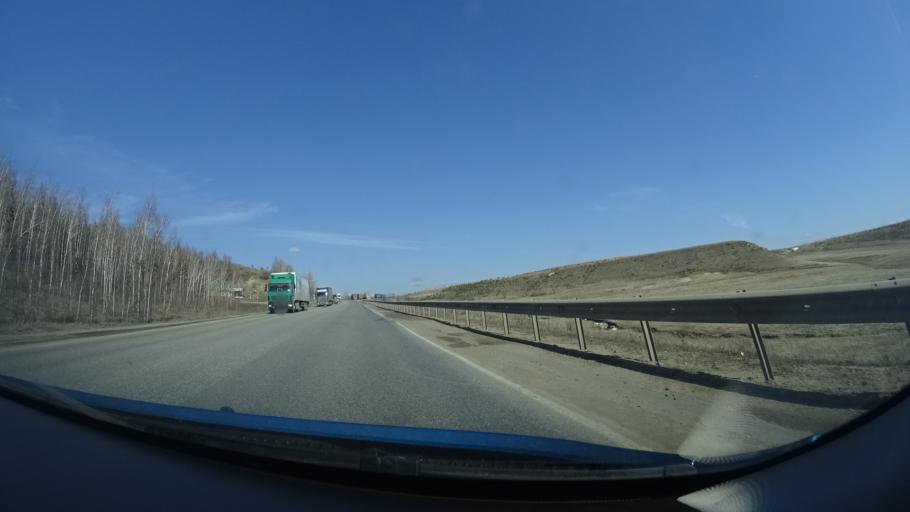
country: RU
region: Bashkortostan
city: Subkhankulovo
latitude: 54.4978
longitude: 53.9399
